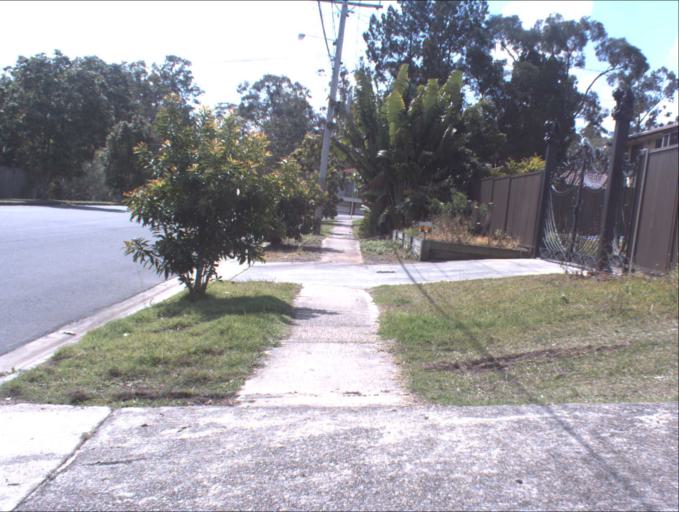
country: AU
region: Queensland
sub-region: Brisbane
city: Sunnybank Hills
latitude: -27.6562
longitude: 153.0456
